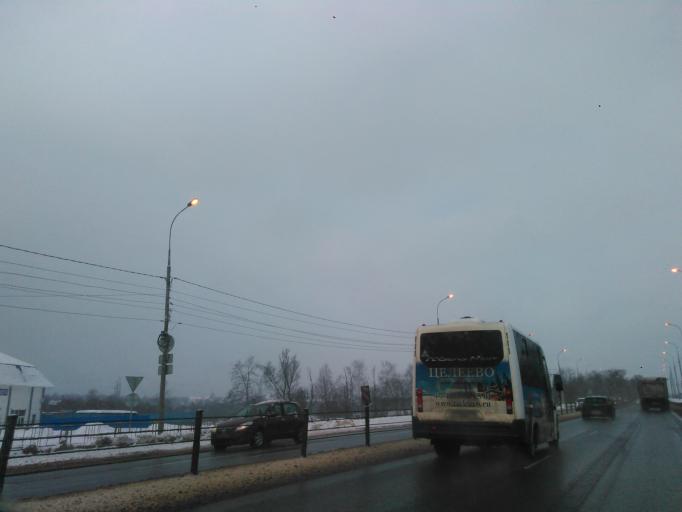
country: RU
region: Moskovskaya
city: Podosinki
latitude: 56.2093
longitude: 37.5225
